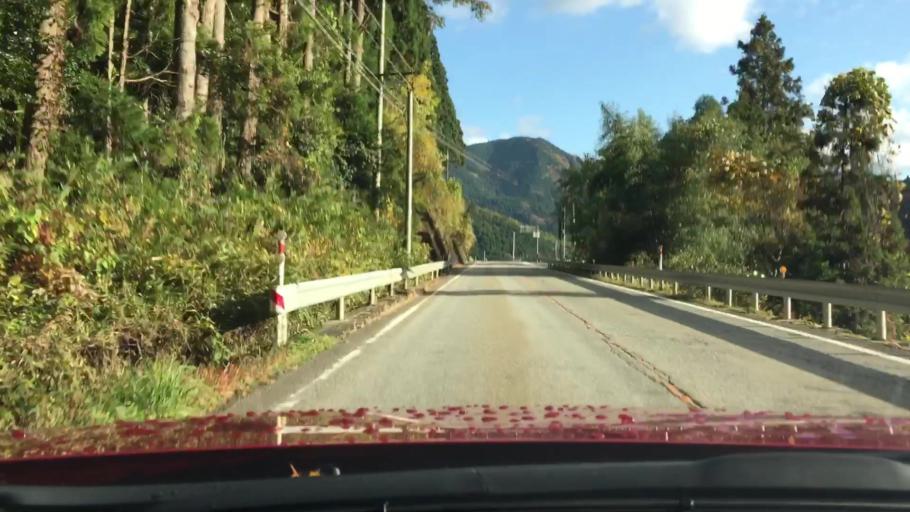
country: JP
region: Hyogo
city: Yamazakicho-nakabirose
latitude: 35.1774
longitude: 134.5376
